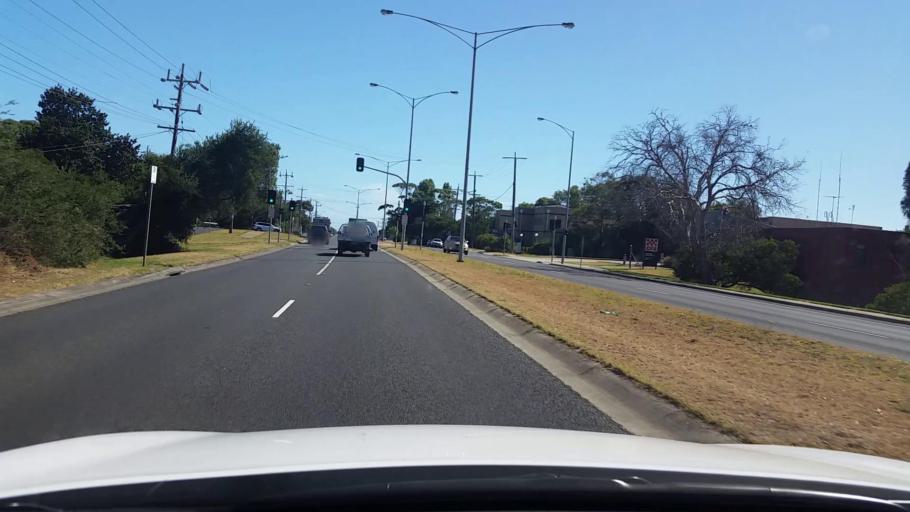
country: AU
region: Victoria
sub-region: Mornington Peninsula
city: Rosebud West
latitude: -38.3709
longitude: 144.8893
